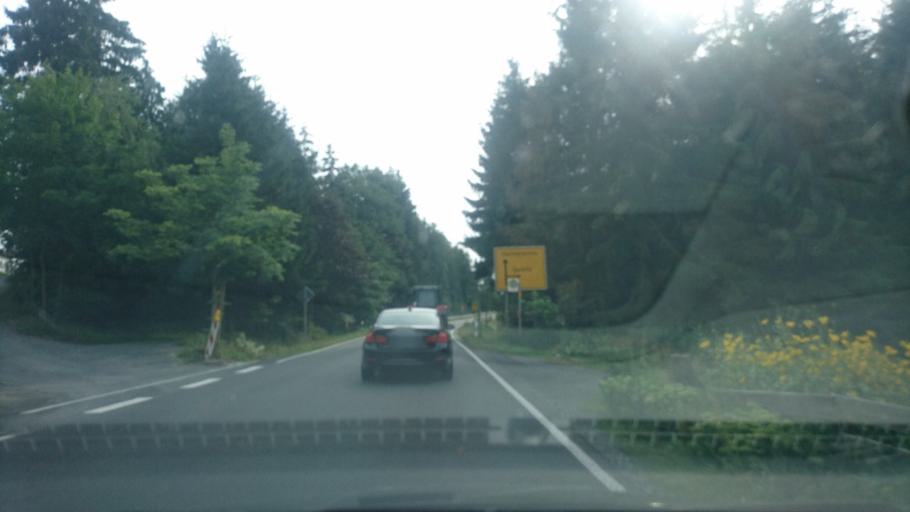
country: DE
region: Bavaria
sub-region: Upper Franconia
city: Leupoldsgrun
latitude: 50.2858
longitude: 11.7855
